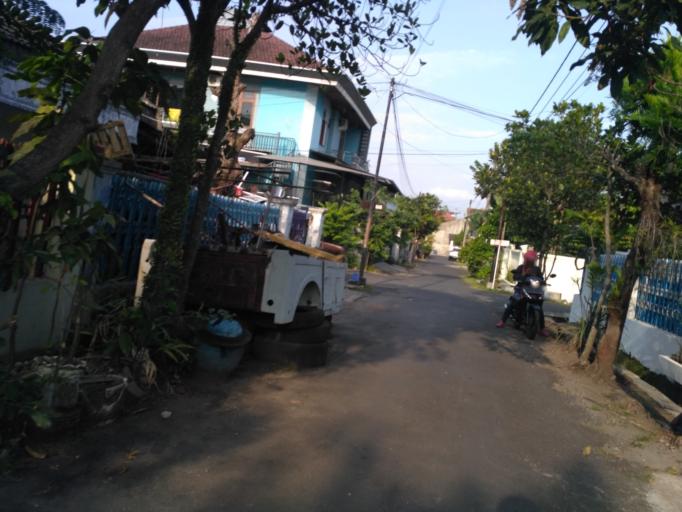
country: ID
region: East Java
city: Malang
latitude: -7.9402
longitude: 112.6285
